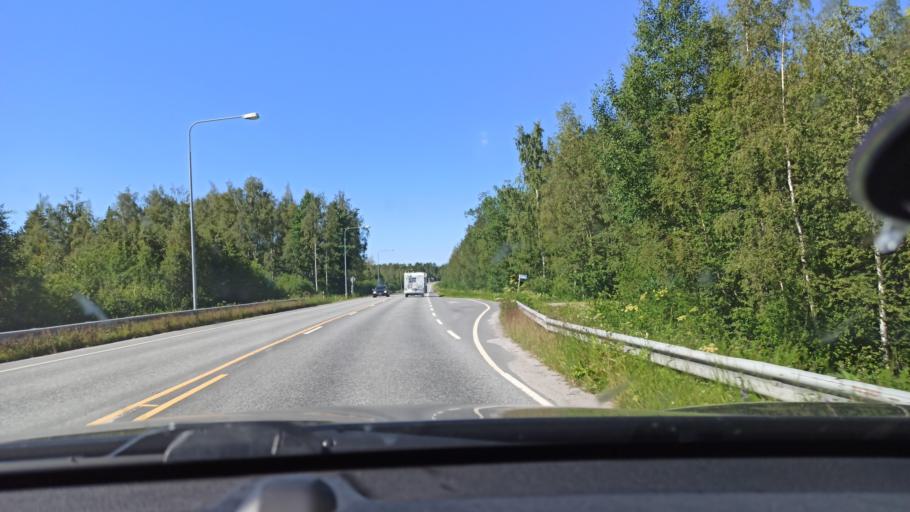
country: FI
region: Ostrobothnia
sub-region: Jakobstadsregionen
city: Jakobstad
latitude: 63.6603
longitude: 22.7100
